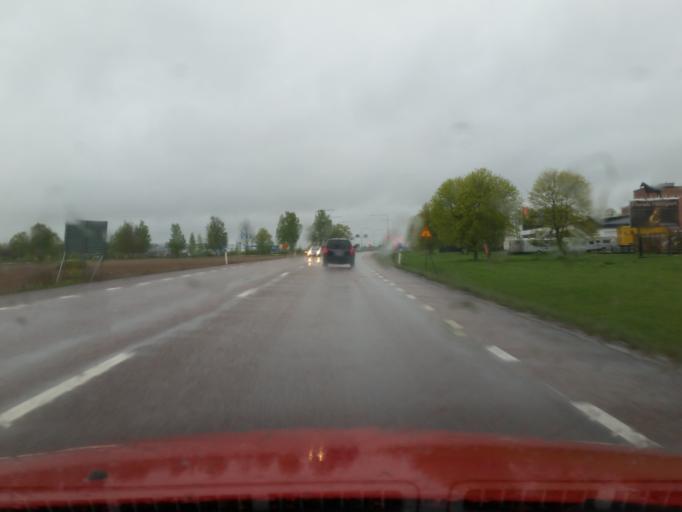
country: SE
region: Dalarna
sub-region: Borlange Kommun
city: Borlaenge
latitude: 60.4661
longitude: 15.4686
